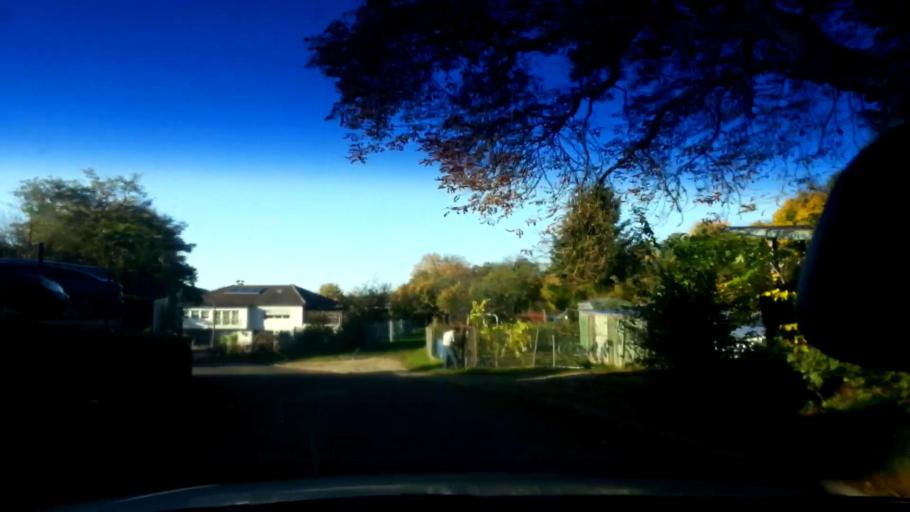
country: DE
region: Bavaria
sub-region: Upper Franconia
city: Rattelsdorf
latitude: 50.0175
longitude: 10.8888
